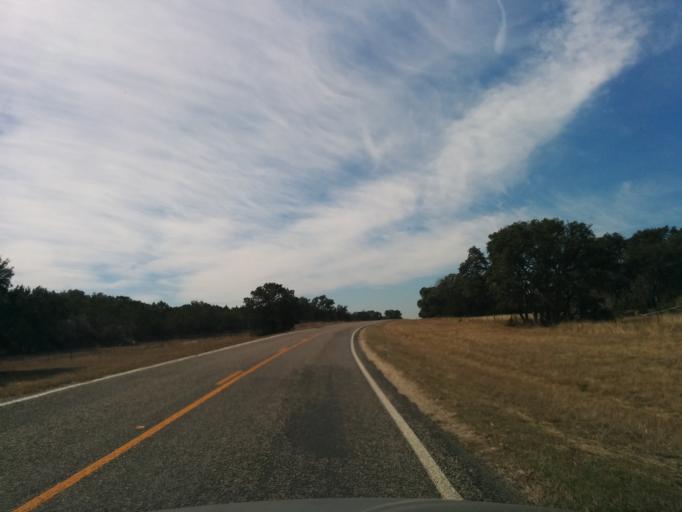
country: US
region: Texas
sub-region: Blanco County
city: Blanco
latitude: 29.9590
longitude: -98.5400
